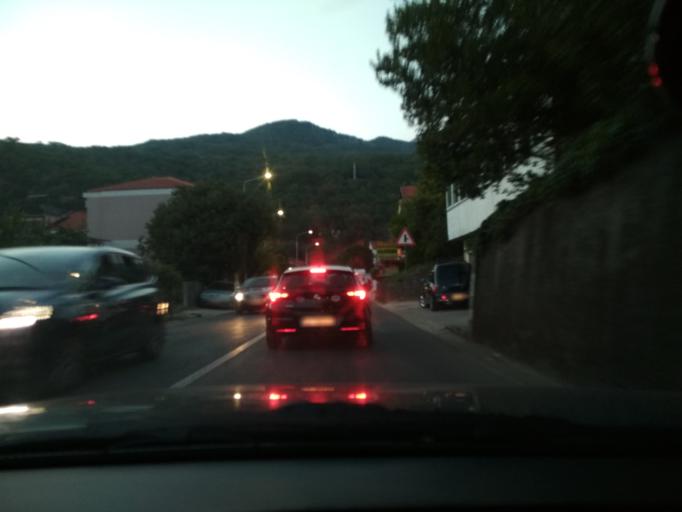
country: ME
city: Igalo
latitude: 42.4601
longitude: 18.5210
